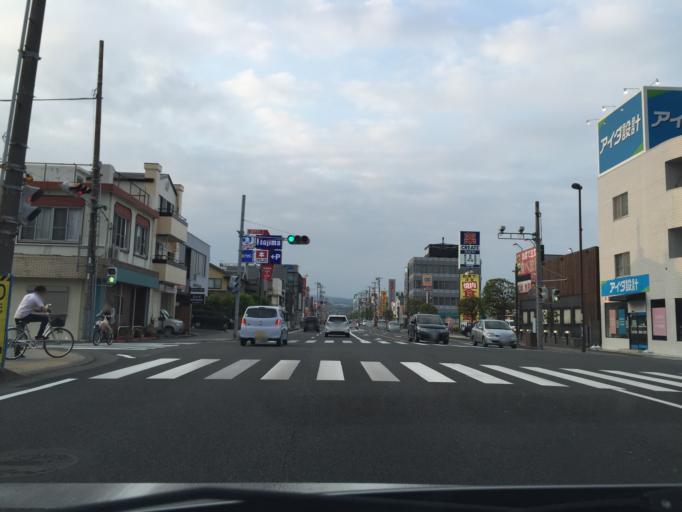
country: JP
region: Shizuoka
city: Numazu
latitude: 35.1110
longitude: 138.8591
